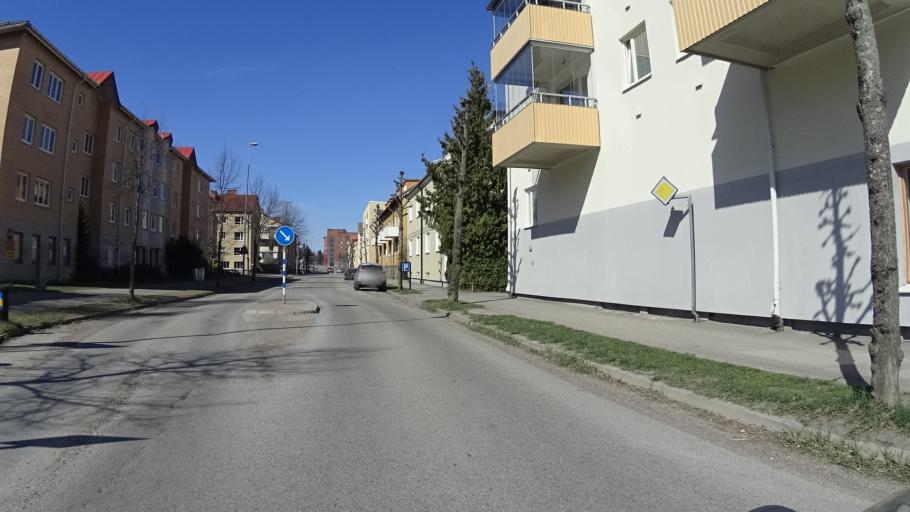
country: SE
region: Soedermanland
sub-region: Katrineholms Kommun
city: Katrineholm
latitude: 58.9906
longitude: 16.2156
